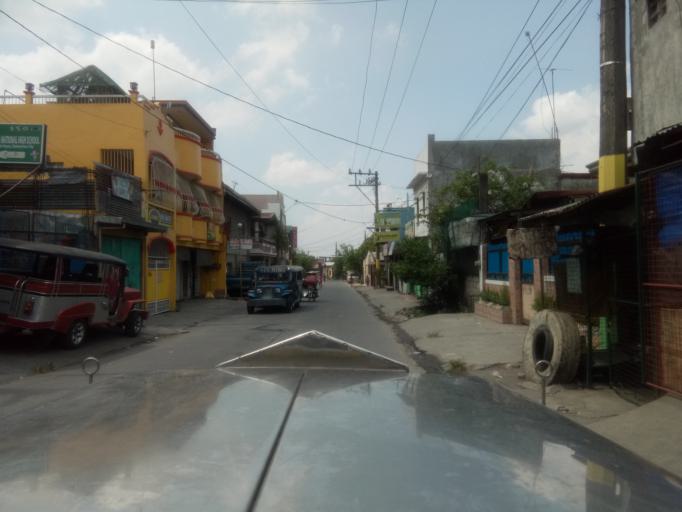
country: PH
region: Calabarzon
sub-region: Province of Cavite
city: Bulihan
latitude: 14.3143
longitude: 120.9765
